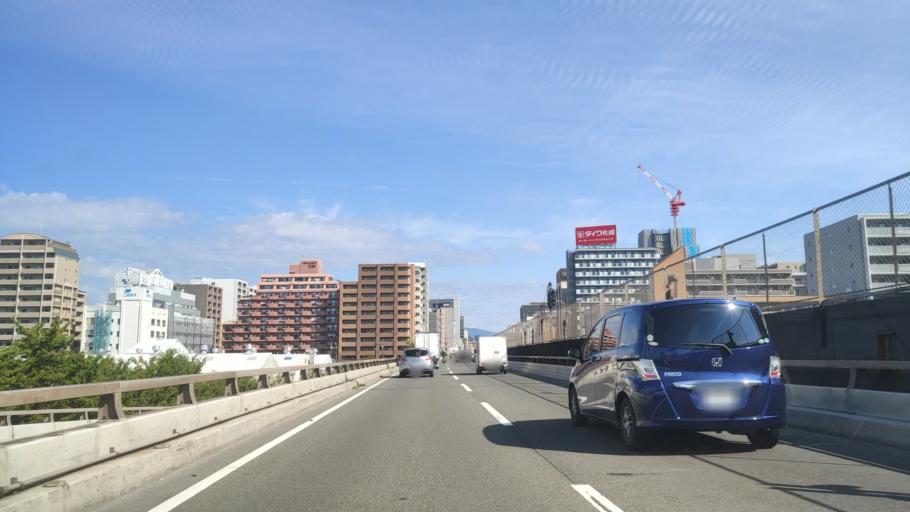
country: JP
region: Osaka
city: Suita
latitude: 34.7526
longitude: 135.4966
